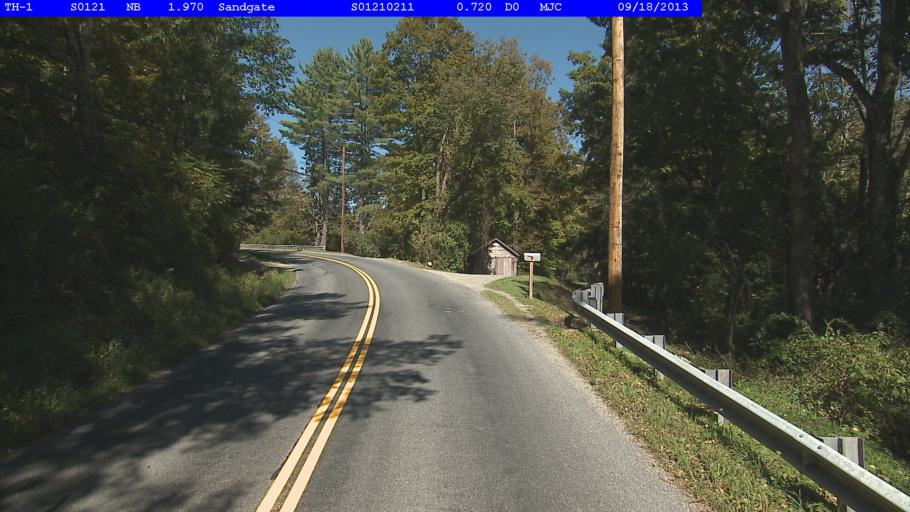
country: US
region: Vermont
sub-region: Bennington County
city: Arlington
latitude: 43.1306
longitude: -73.2047
